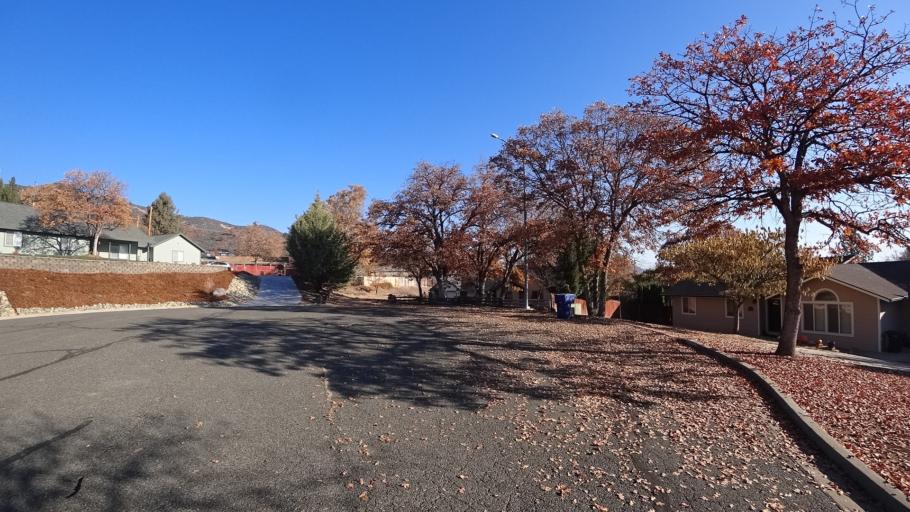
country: US
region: California
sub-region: Siskiyou County
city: Yreka
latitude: 41.7412
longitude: -122.6499
